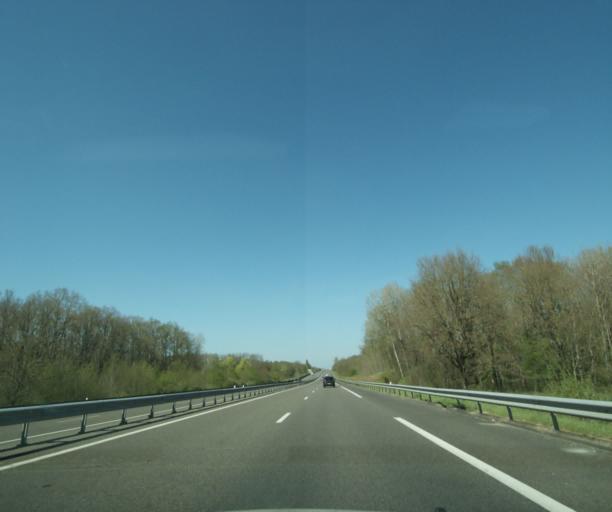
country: FR
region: Bourgogne
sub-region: Departement de la Nievre
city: Cosne-Cours-sur-Loire
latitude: 47.3632
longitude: 2.9237
